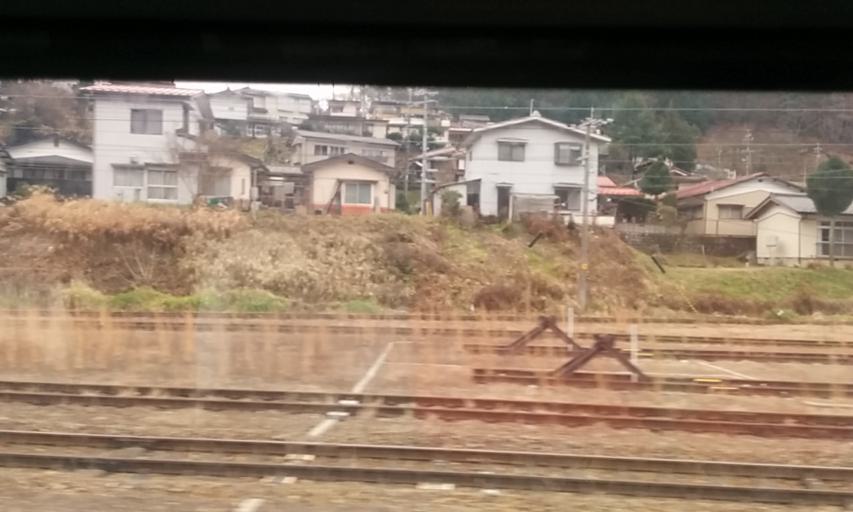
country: JP
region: Nagano
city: Ina
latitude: 35.8452
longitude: 137.6938
